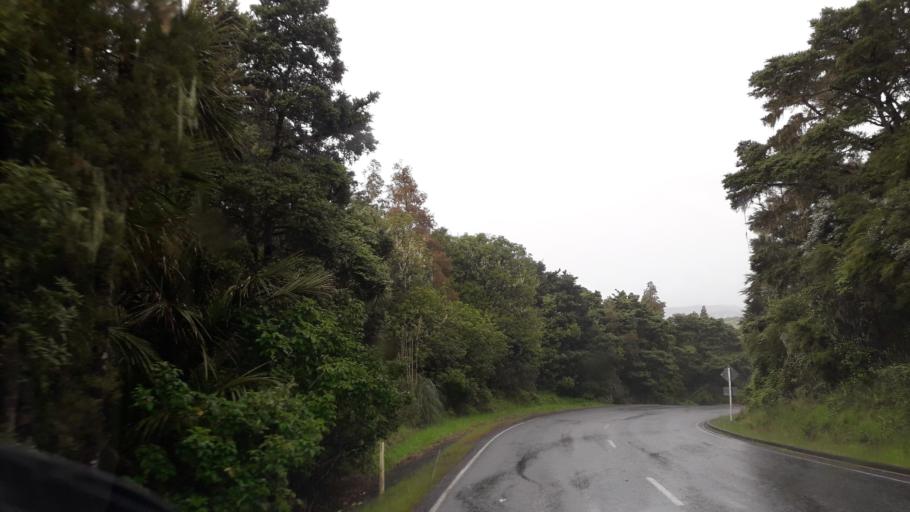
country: NZ
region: Northland
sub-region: Far North District
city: Kaitaia
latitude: -35.3577
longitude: 173.4965
